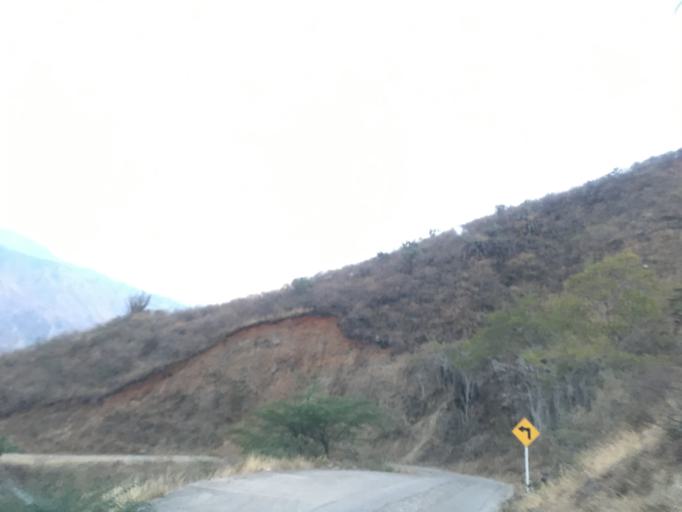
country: CO
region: Santander
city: Aratoca
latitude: 6.7824
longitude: -72.9955
